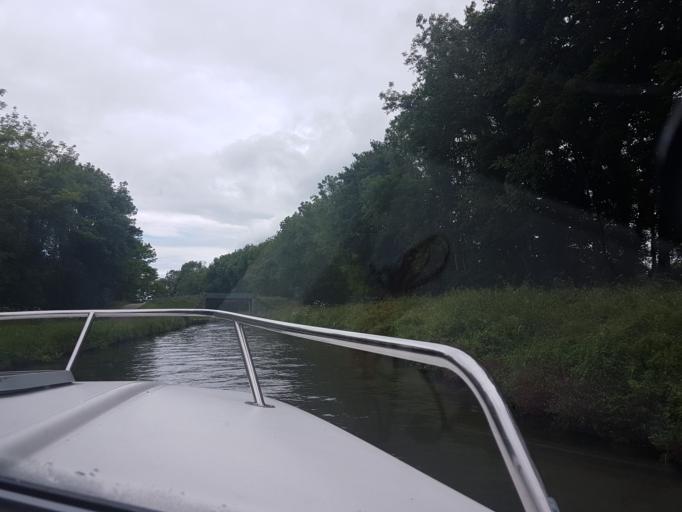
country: FR
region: Bourgogne
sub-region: Departement de l'Yonne
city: Vermenton
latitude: 47.6480
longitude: 3.6661
